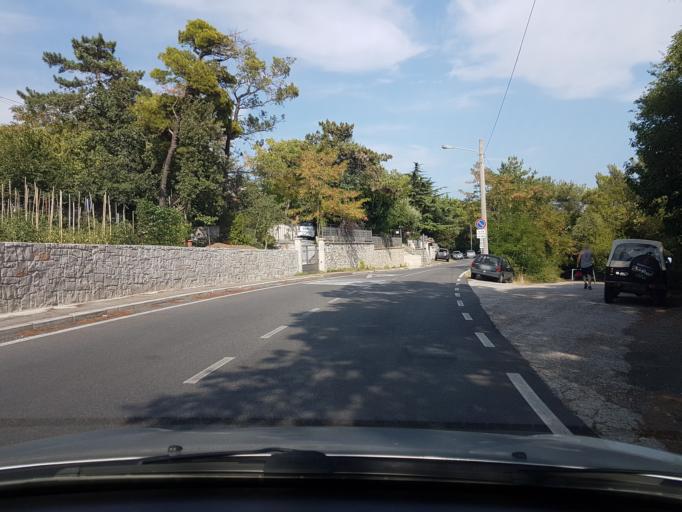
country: IT
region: Friuli Venezia Giulia
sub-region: Provincia di Trieste
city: Sistiana-Visogliano
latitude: 45.7727
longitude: 13.6301
